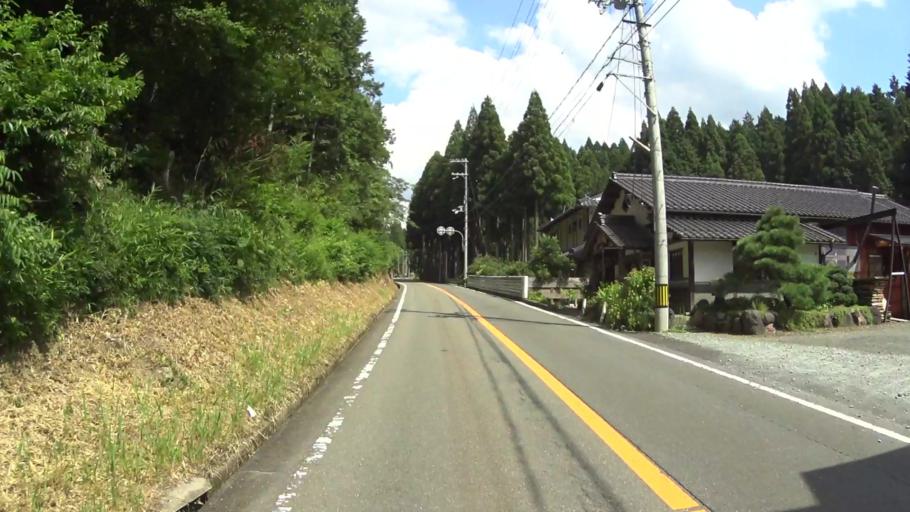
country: JP
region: Kyoto
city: Kameoka
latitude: 35.2777
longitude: 135.5561
